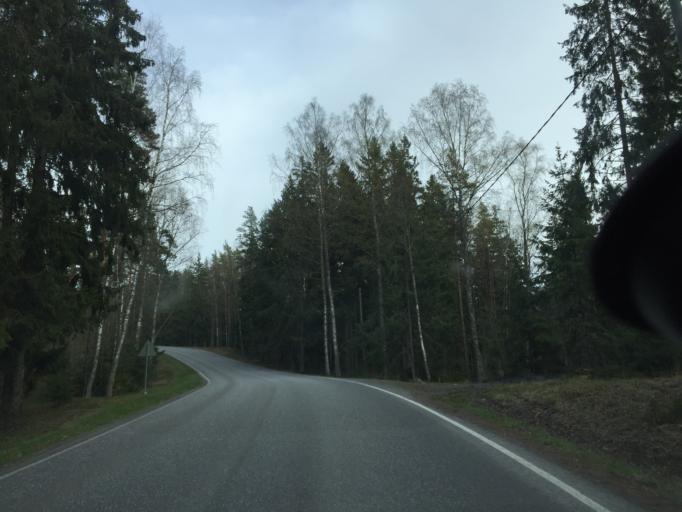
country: FI
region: Varsinais-Suomi
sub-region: Salo
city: Pernioe
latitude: 60.0065
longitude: 23.1173
